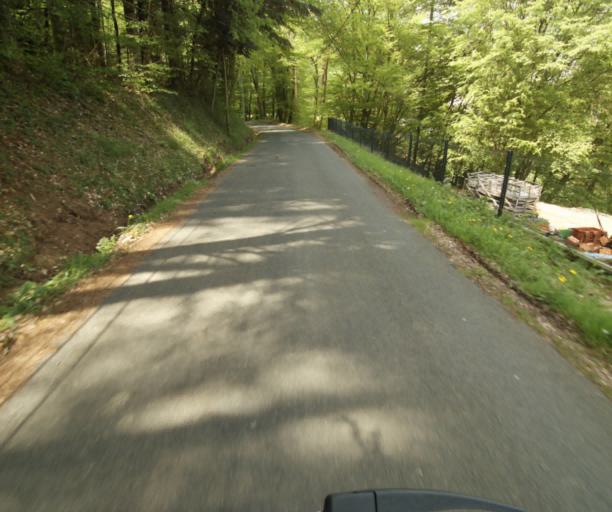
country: FR
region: Limousin
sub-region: Departement de la Correze
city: Tulle
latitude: 45.2755
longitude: 1.7599
